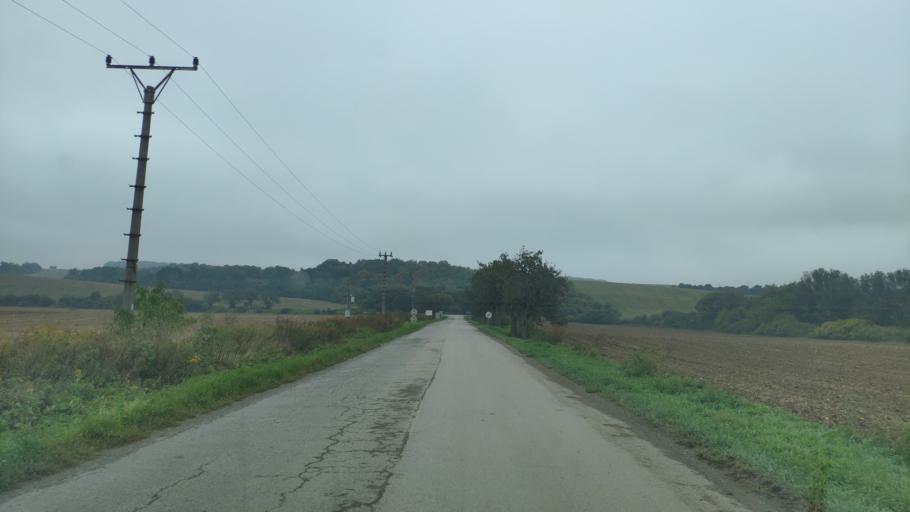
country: SK
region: Kosicky
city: Kosice
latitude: 48.7709
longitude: 21.3264
